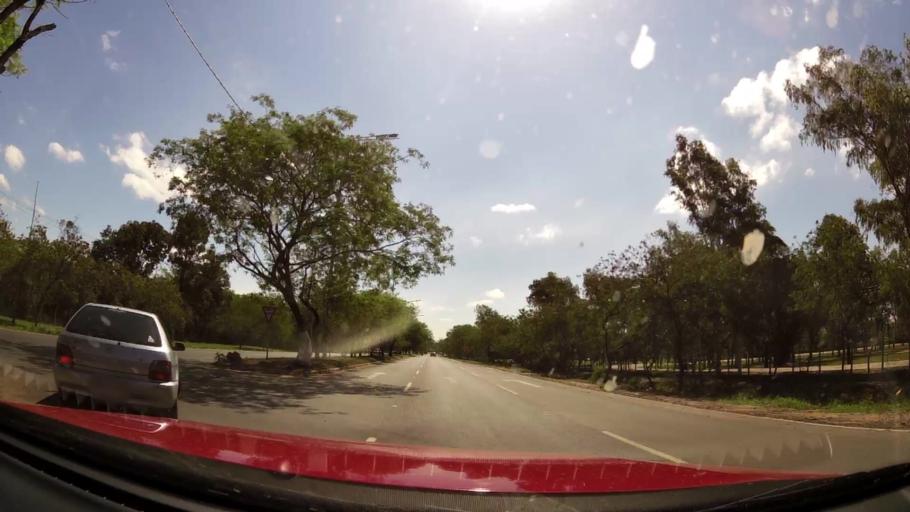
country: PY
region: Central
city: Fernando de la Mora
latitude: -25.2628
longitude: -57.5246
